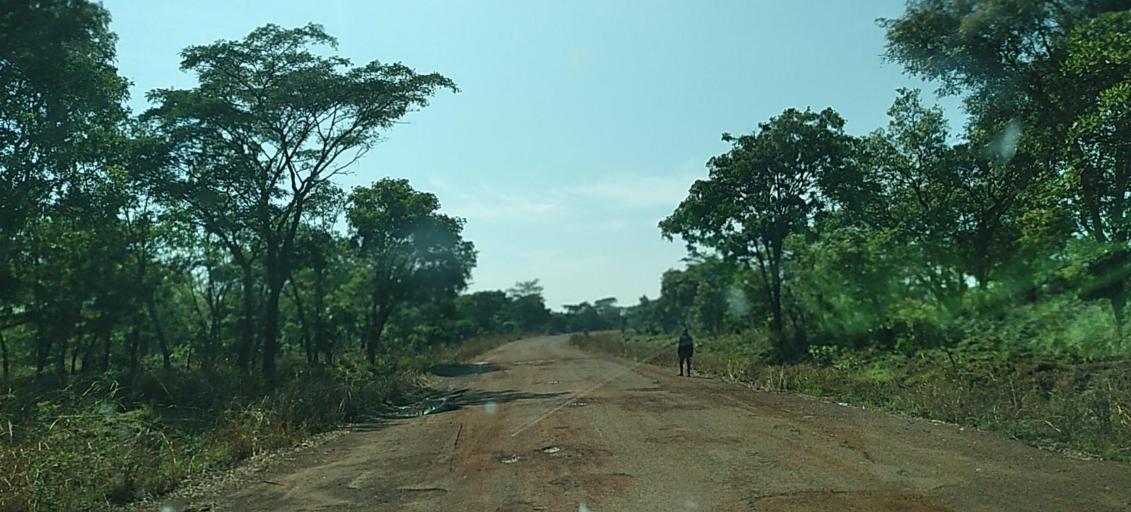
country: ZM
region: North-Western
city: Mwinilunga
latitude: -11.7915
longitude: 25.0682
